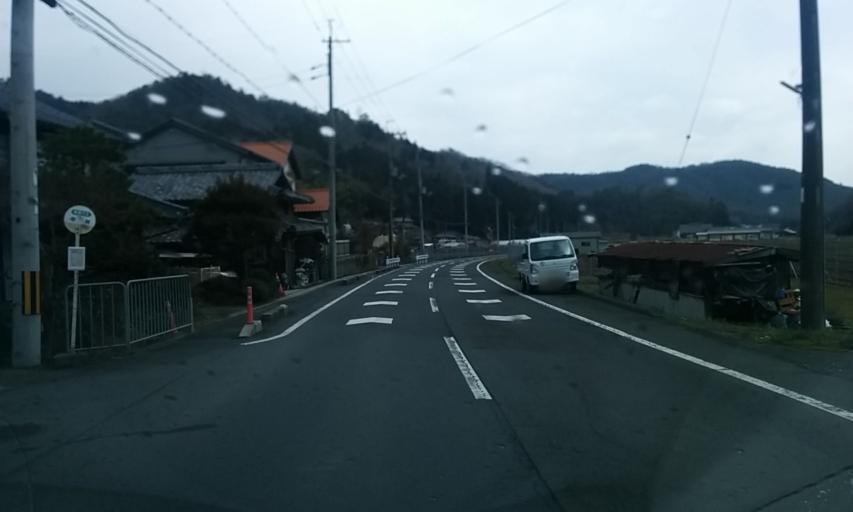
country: JP
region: Hyogo
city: Sasayama
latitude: 35.1292
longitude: 135.4117
